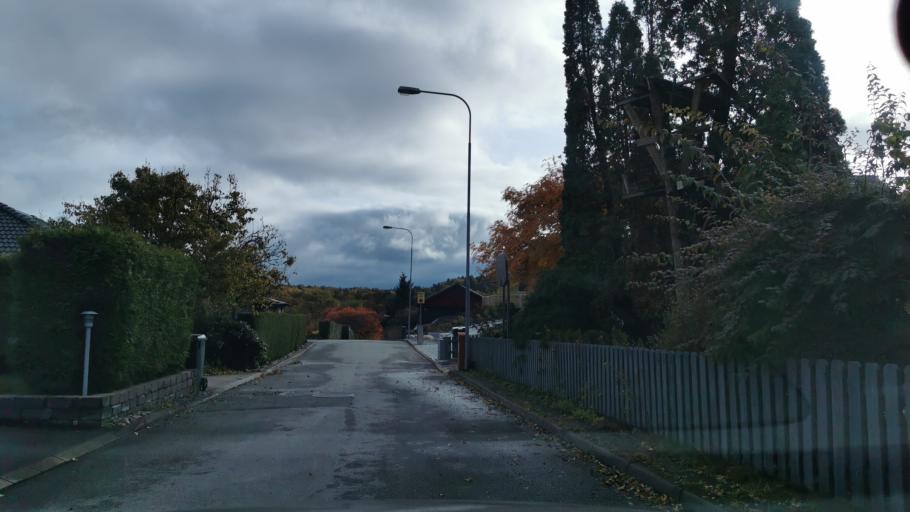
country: SE
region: Vaestra Goetaland
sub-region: Partille Kommun
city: Partille
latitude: 57.7259
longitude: 12.0863
